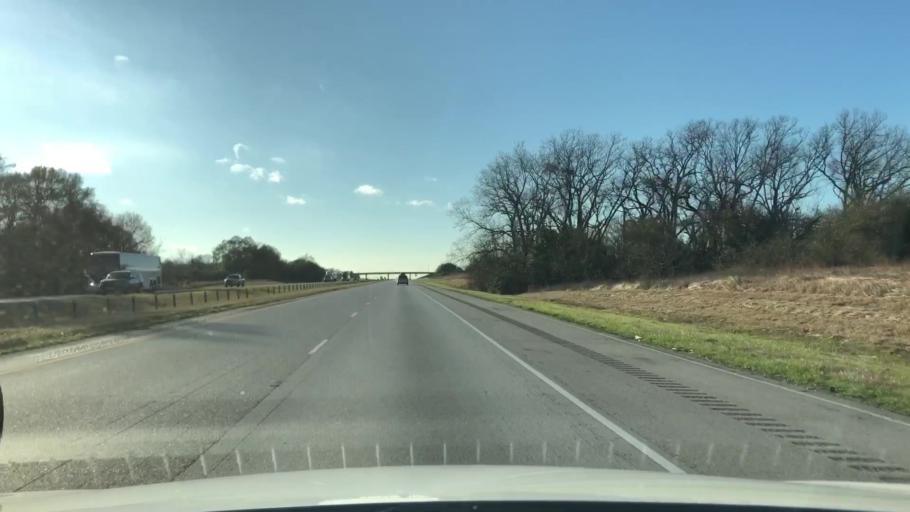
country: US
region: Texas
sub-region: Colorado County
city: Weimar
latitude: 29.6902
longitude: -96.8001
